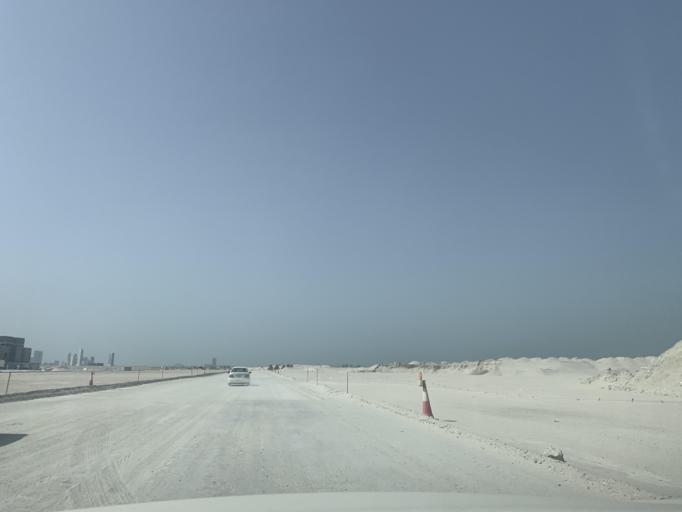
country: BH
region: Northern
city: Sitrah
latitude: 26.1650
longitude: 50.6362
